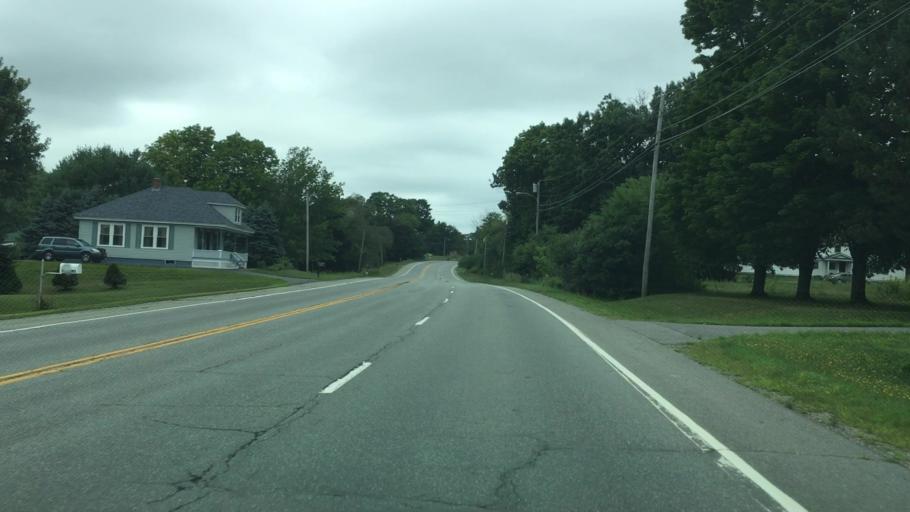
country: US
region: Maine
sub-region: Penobscot County
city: Orrington
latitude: 44.7043
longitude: -68.8449
